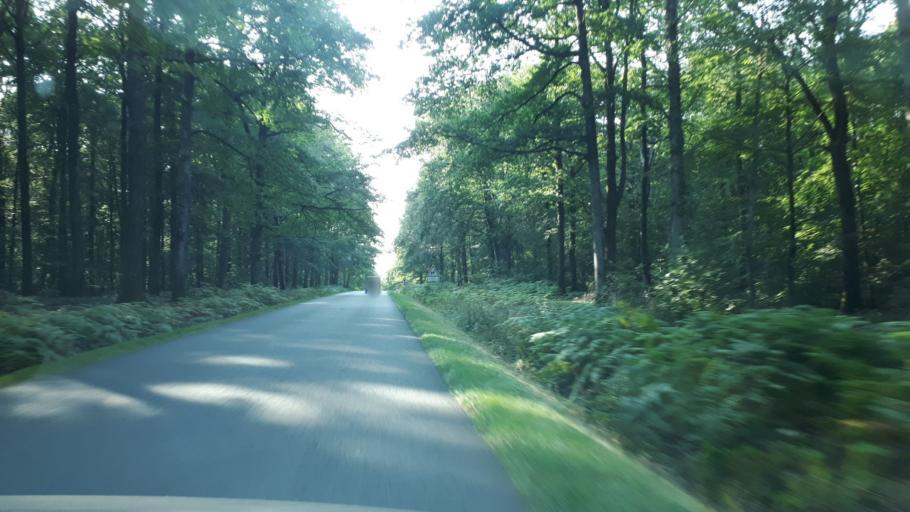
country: FR
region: Centre
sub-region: Departement du Cher
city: Saint-Eloy-de-Gy
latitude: 47.2189
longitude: 2.3534
